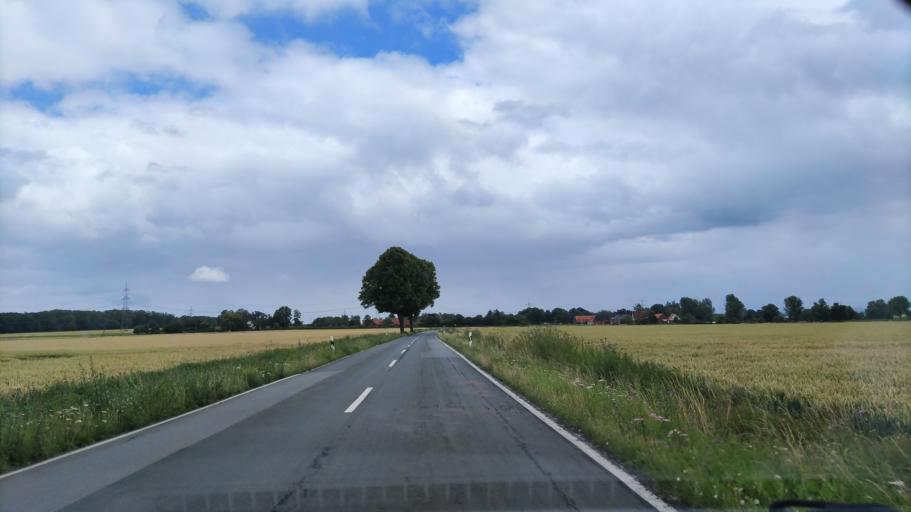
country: DE
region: North Rhine-Westphalia
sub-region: Regierungsbezirk Arnsberg
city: Welver
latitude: 51.6388
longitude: 7.9918
